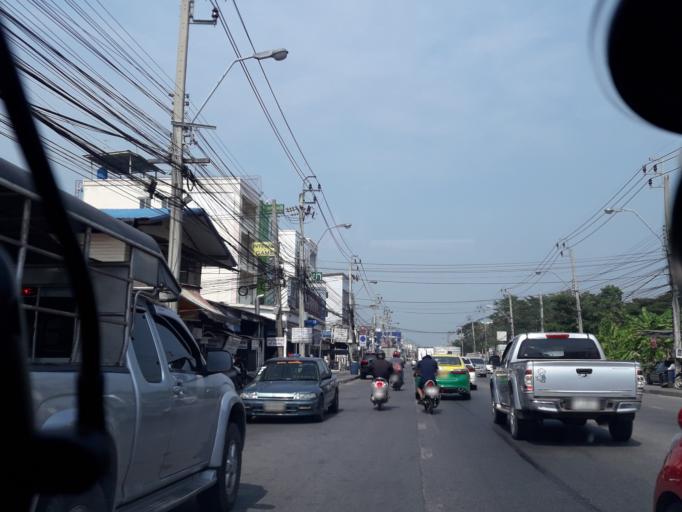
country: TH
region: Bangkok
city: Min Buri
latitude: 13.8249
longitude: 100.7203
